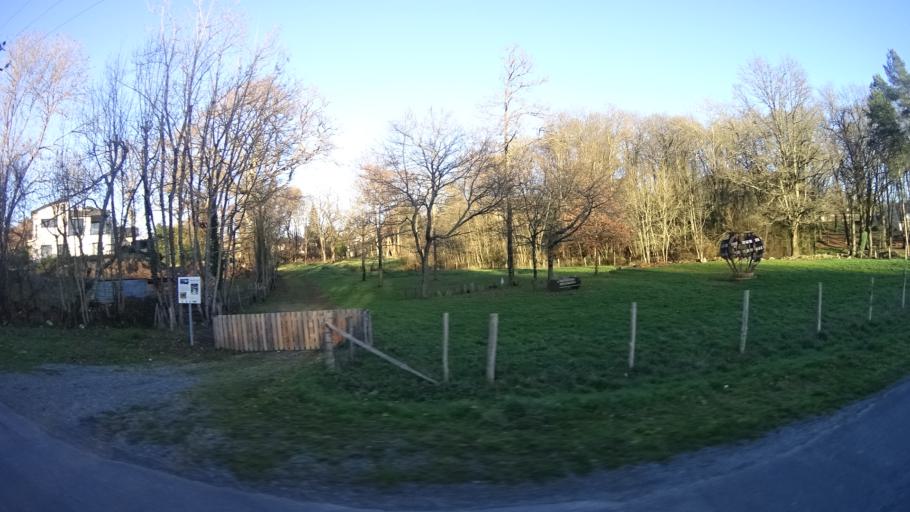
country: FR
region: Brittany
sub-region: Departement du Morbihan
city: Saint-Jean-la-Poterie
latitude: 47.6334
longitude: -2.1233
